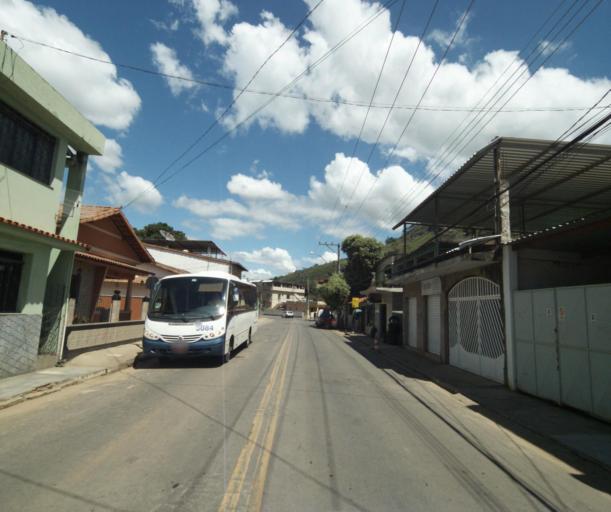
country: BR
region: Espirito Santo
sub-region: Mimoso Do Sul
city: Mimoso do Sul
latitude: -21.0680
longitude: -41.3581
